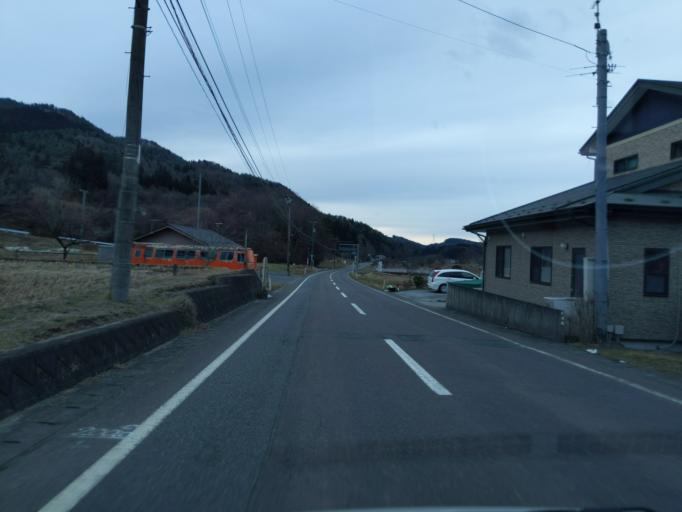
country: JP
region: Iwate
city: Mizusawa
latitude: 39.0589
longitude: 141.2876
